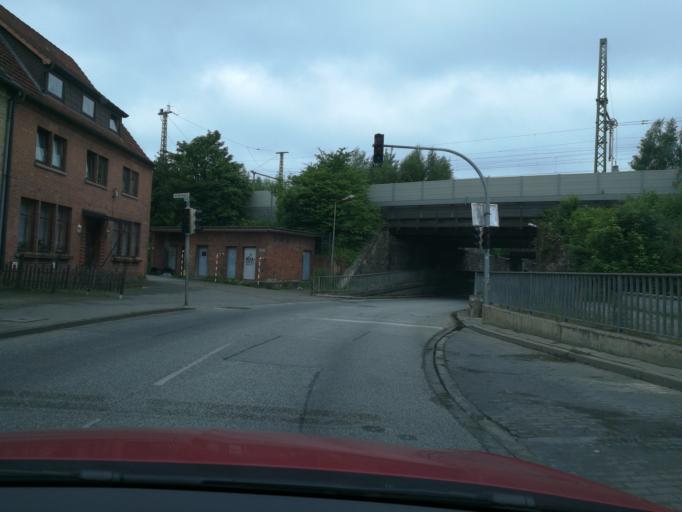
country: DE
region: Schleswig-Holstein
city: Bad Oldesloe
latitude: 53.8028
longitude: 10.3810
